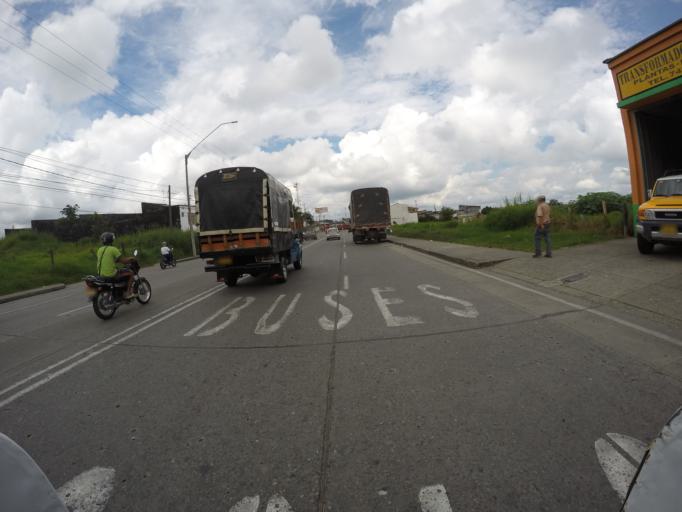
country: CO
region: Quindio
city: Armenia
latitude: 4.5243
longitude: -75.6846
